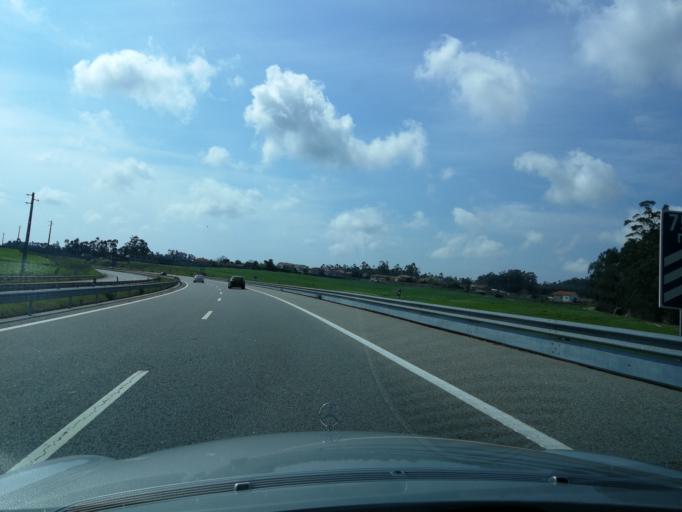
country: PT
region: Porto
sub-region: Vila do Conde
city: Arvore
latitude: 41.3937
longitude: -8.6855
